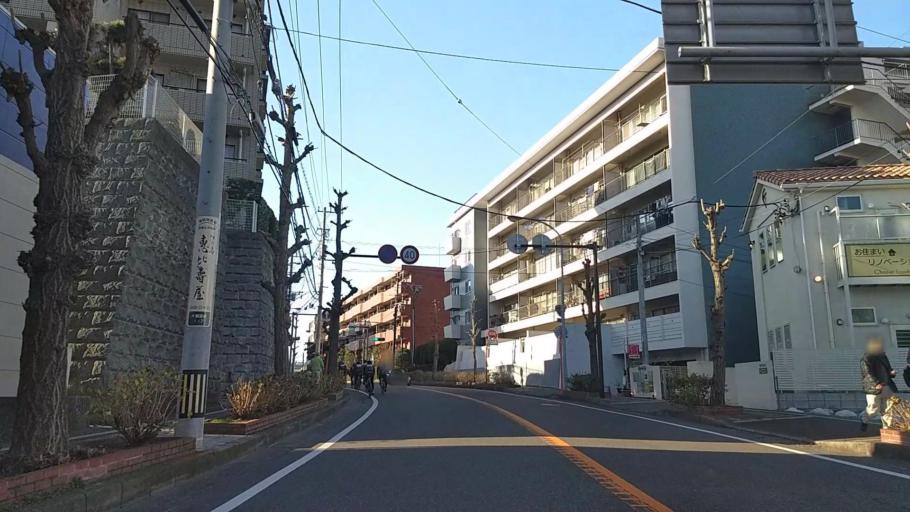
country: JP
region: Kanagawa
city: Fujisawa
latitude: 35.3103
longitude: 139.4886
